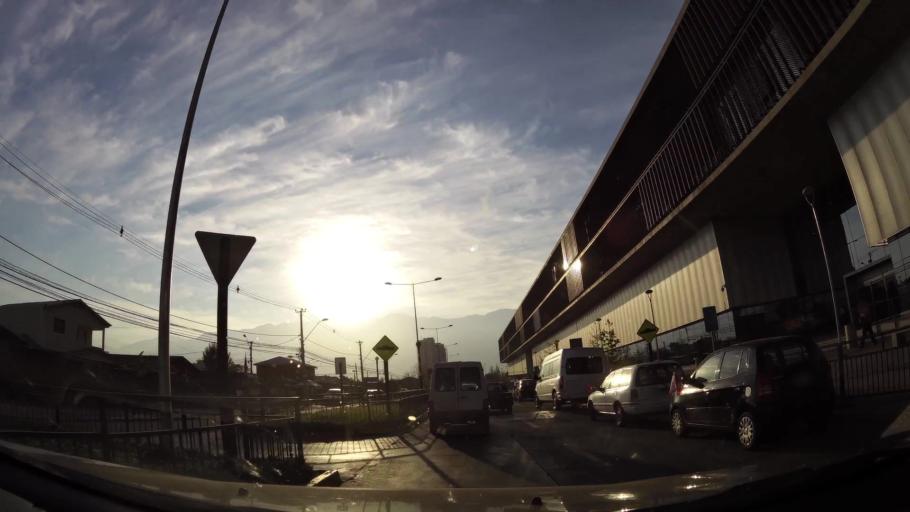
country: CL
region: Santiago Metropolitan
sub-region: Provincia de Santiago
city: Villa Presidente Frei, Nunoa, Santiago, Chile
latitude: -33.5139
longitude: -70.5988
